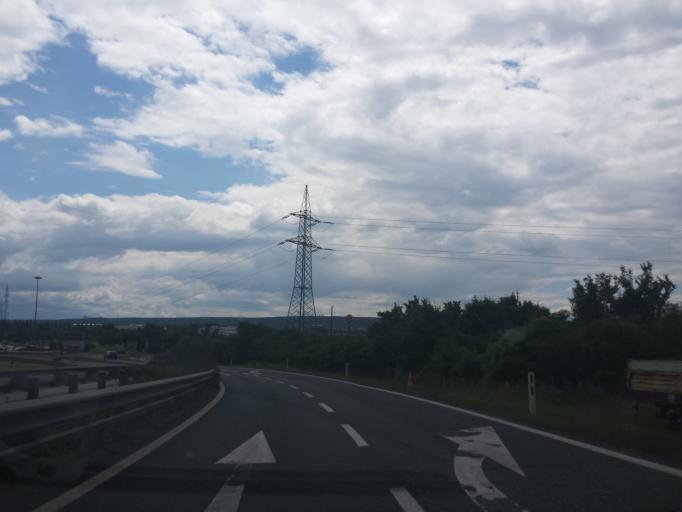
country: AT
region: Lower Austria
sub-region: Politischer Bezirk Baden
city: Leobersdorf
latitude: 47.9334
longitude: 16.2047
